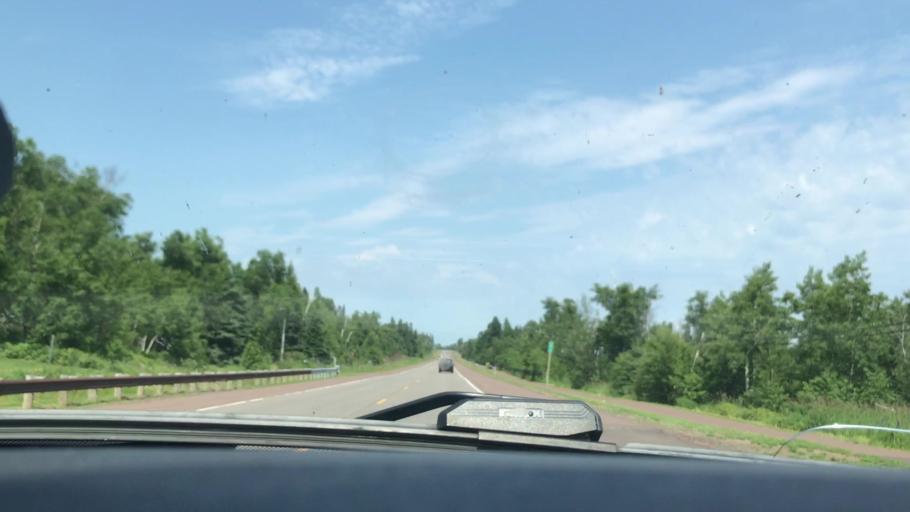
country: US
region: Minnesota
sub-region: Cook County
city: Grand Marais
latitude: 47.5866
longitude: -90.8123
